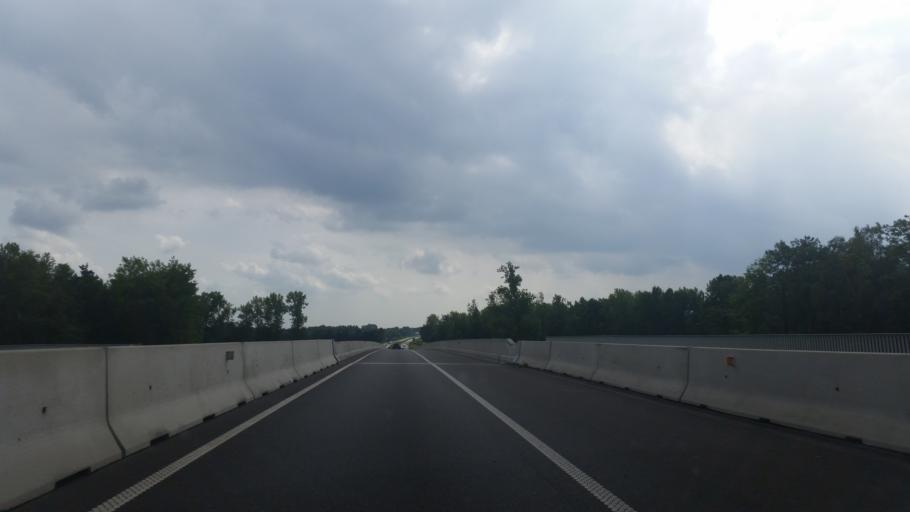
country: BE
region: Flanders
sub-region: Provincie Antwerpen
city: Geel
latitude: 51.1990
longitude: 4.9704
